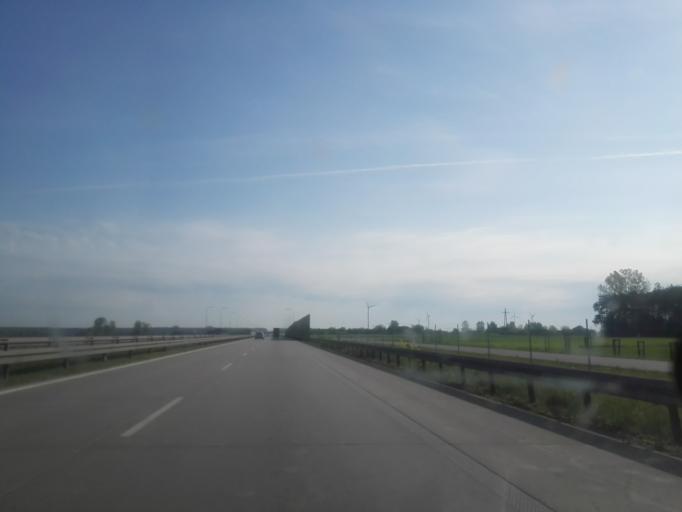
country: PL
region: Lodz Voivodeship
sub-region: Powiat piotrkowski
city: Wolborz
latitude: 51.4676
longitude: 19.7925
